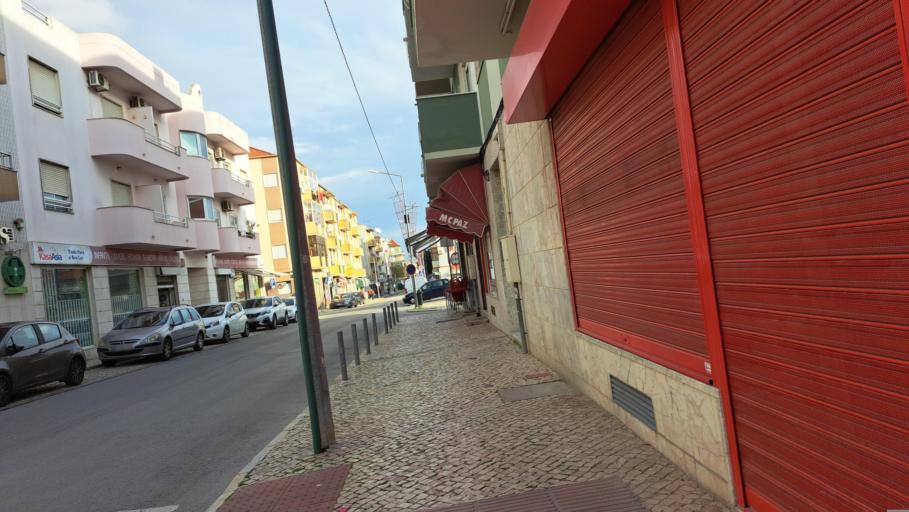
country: PT
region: Setubal
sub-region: Moita
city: Alhos Vedros
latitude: 38.6543
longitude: -9.0444
